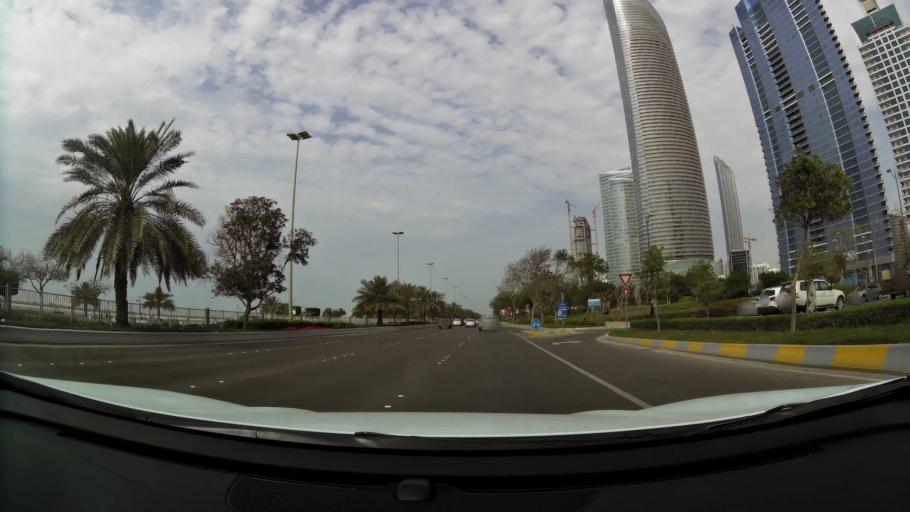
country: AE
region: Abu Dhabi
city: Abu Dhabi
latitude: 24.4826
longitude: 54.3479
